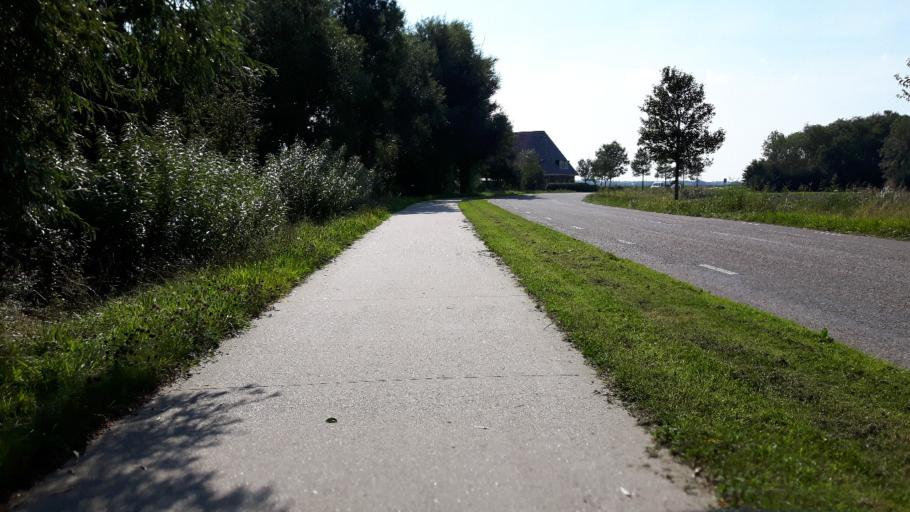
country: NL
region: Friesland
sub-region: Gemeente Franekeradeel
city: Franeker
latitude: 53.2101
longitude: 5.5569
